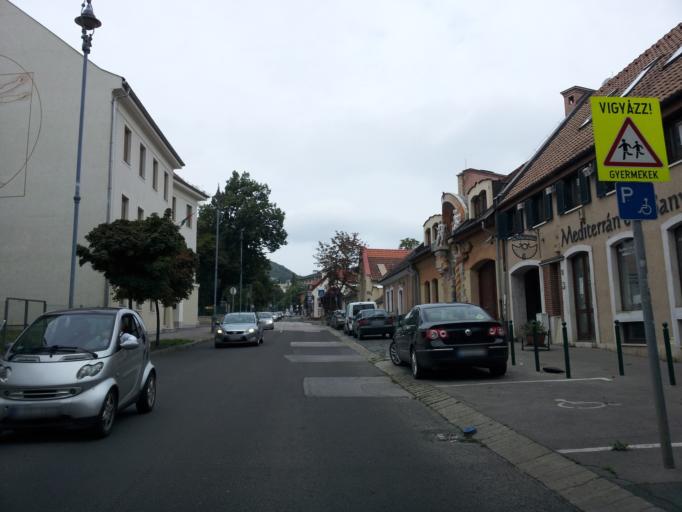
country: HU
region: Budapest
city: Budapest II. keruelet
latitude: 47.5272
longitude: 19.0340
